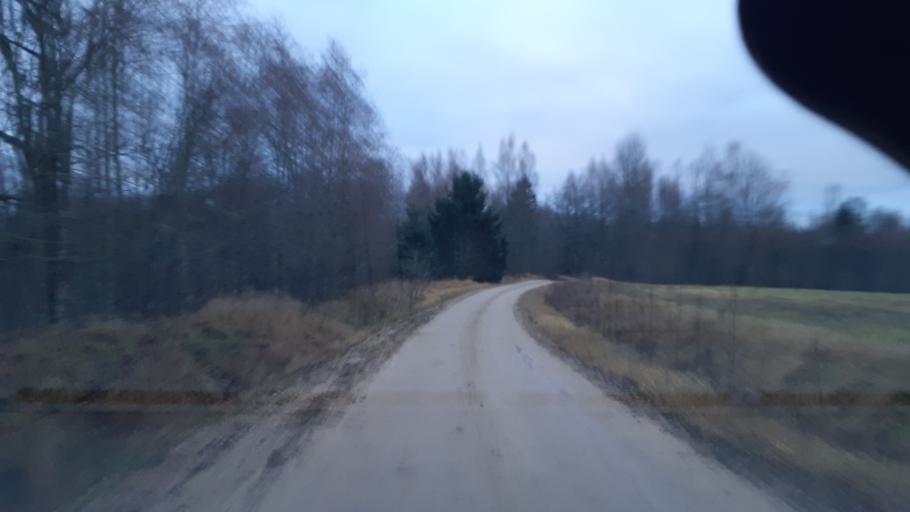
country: LV
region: Alsunga
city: Alsunga
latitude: 56.9172
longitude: 21.7146
